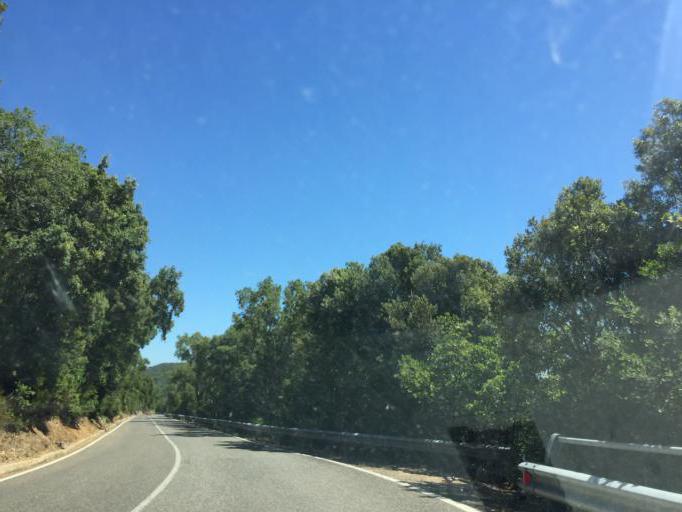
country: IT
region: Sardinia
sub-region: Provincia di Olbia-Tempio
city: Calangianus
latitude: 40.8862
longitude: 9.2590
